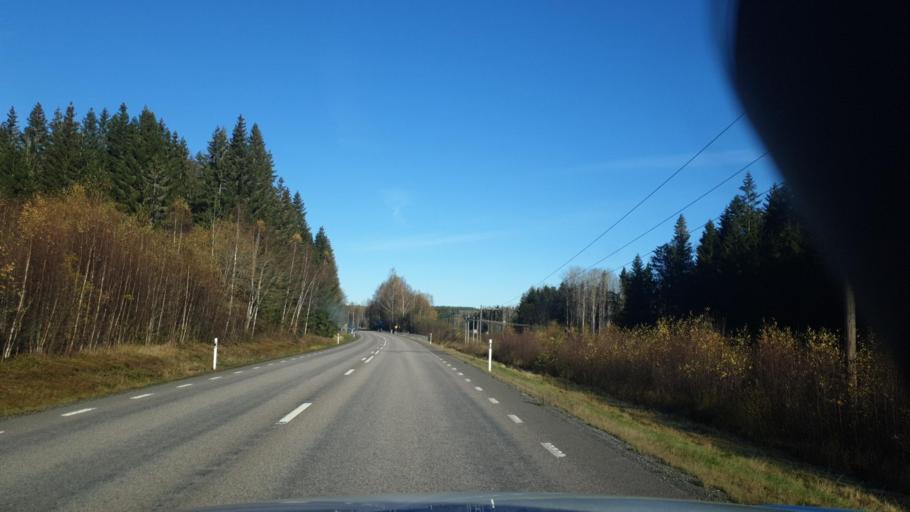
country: SE
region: Vaermland
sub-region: Karlstads Kommun
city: Edsvalla
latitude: 59.4396
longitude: 13.2024
